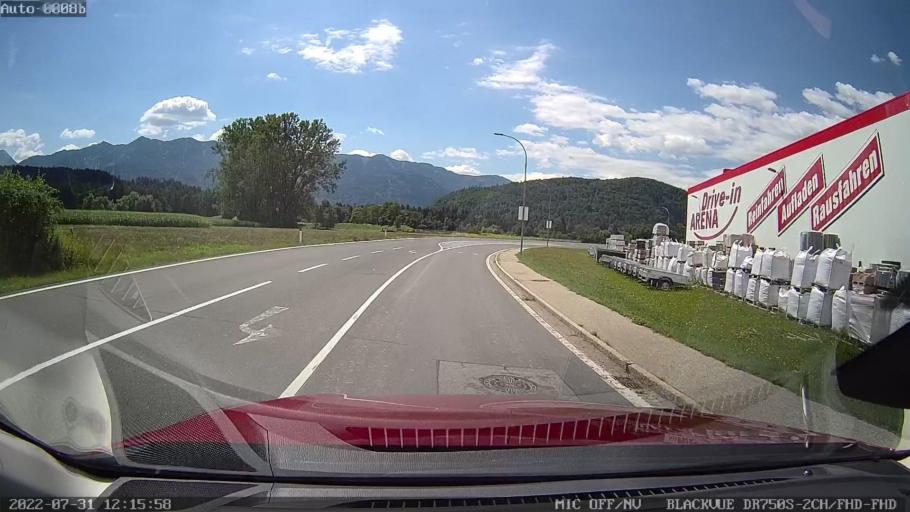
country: AT
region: Carinthia
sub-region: Villach Stadt
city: Villach
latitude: 46.5904
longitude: 13.8383
